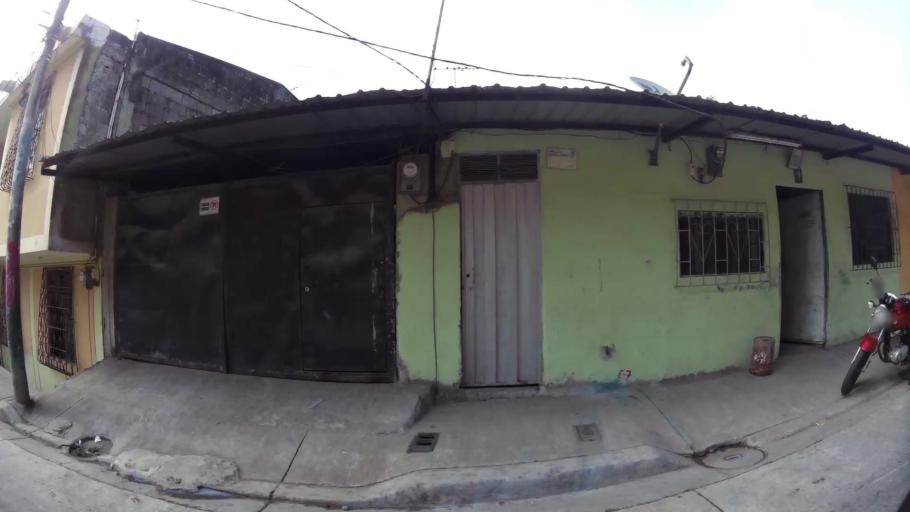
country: EC
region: Guayas
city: Guayaquil
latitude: -2.1500
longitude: -79.9367
